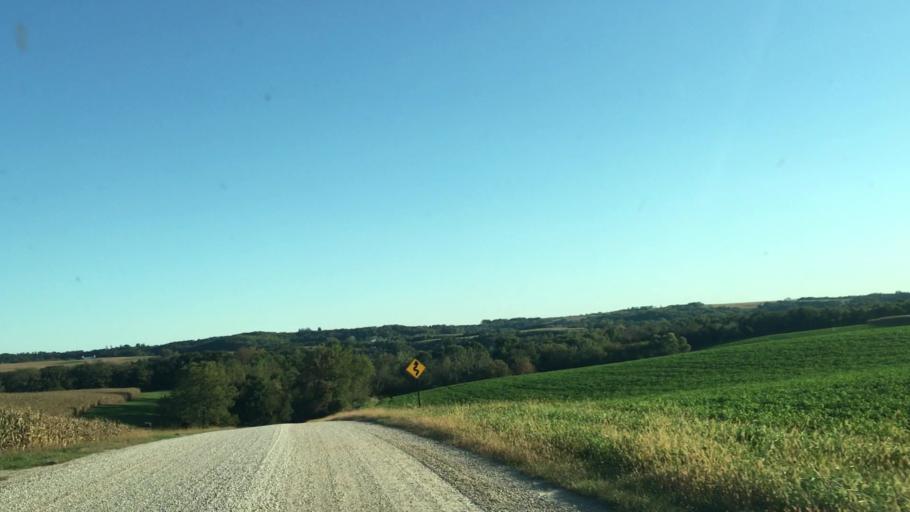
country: US
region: Minnesota
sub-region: Fillmore County
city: Preston
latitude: 43.7677
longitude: -92.0294
